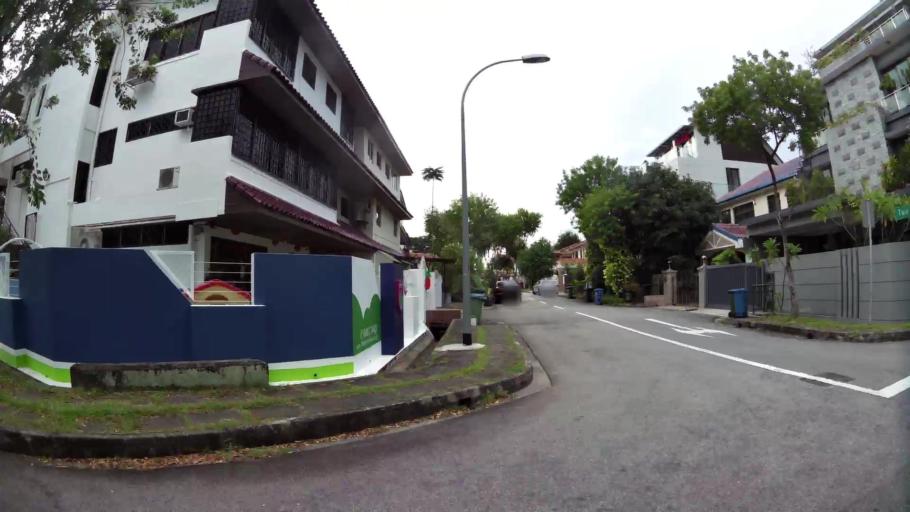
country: SG
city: Singapore
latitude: 1.3814
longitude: 103.8325
